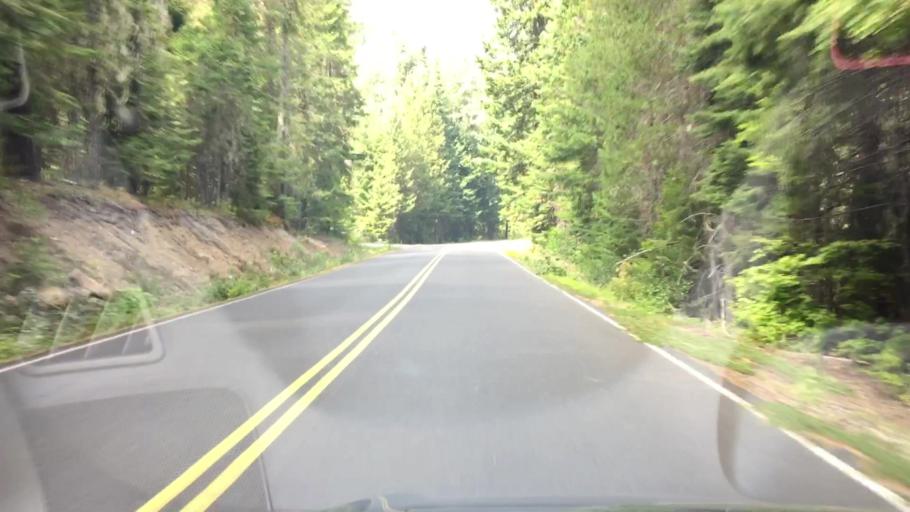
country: US
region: Washington
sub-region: Klickitat County
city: White Salmon
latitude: 46.0553
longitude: -121.5657
